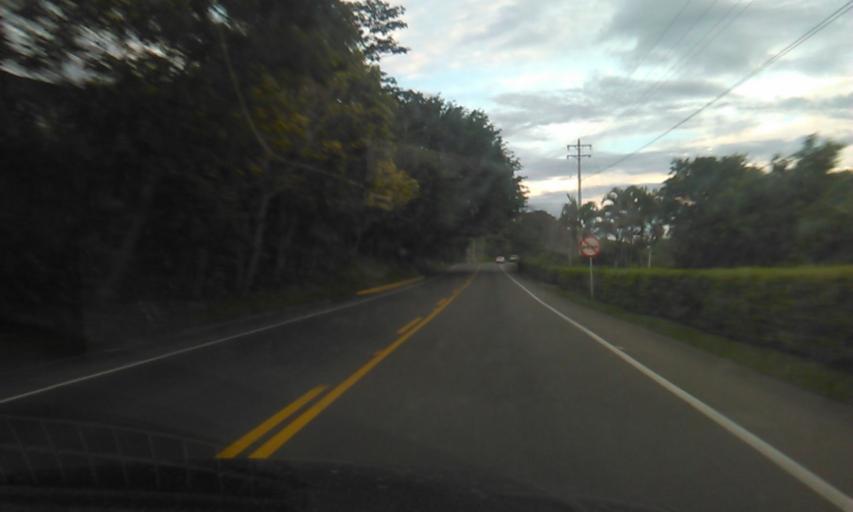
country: CO
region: Quindio
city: La Tebaida
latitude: 4.4276
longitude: -75.8608
